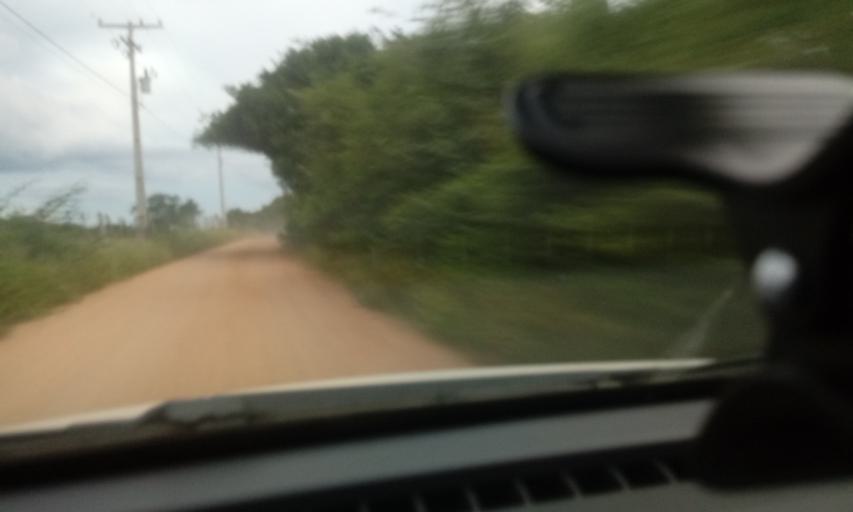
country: BR
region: Bahia
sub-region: Riacho De Santana
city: Riacho de Santana
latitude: -13.8183
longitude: -42.7637
